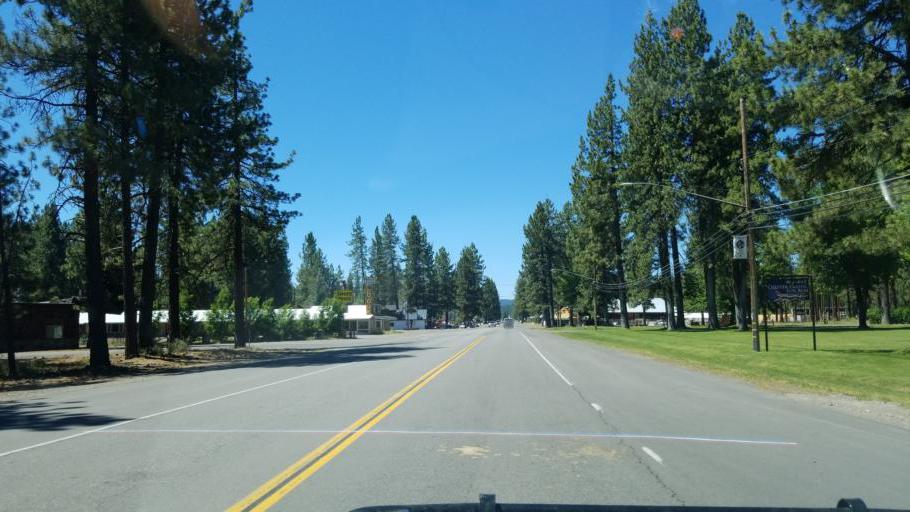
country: US
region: California
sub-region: Plumas County
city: Chester
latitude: 40.3019
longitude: -121.2355
